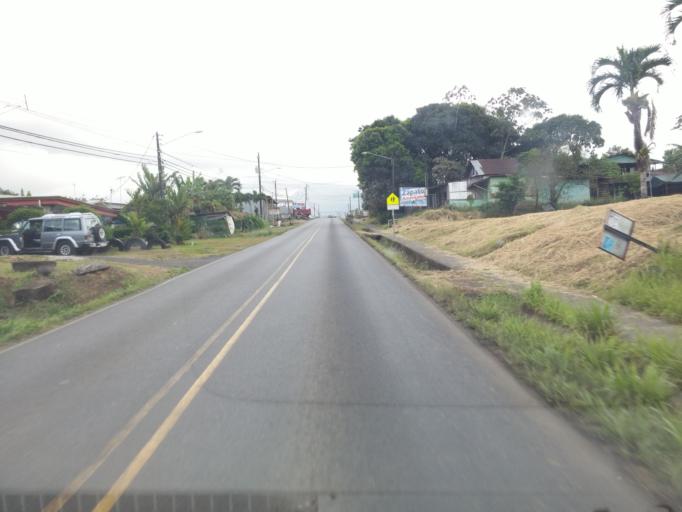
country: CR
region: Alajuela
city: Pital
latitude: 10.3795
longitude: -84.3398
